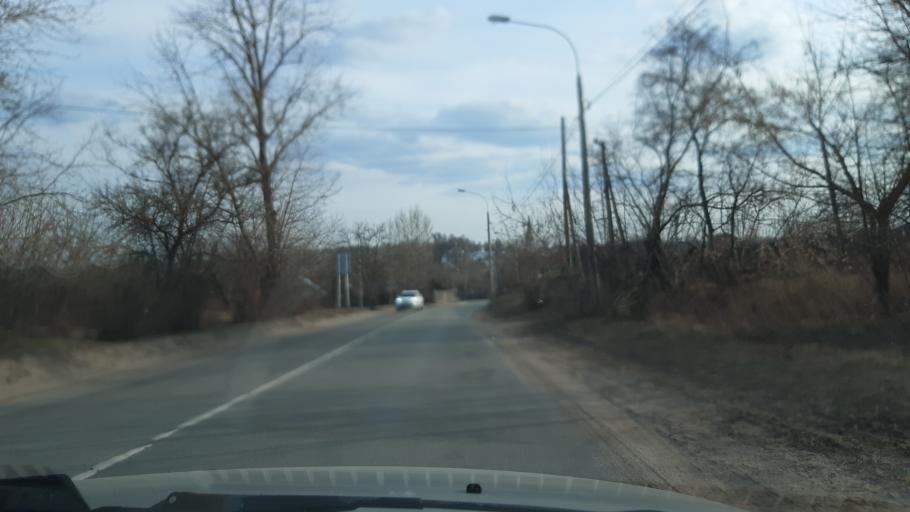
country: RU
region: Vladimir
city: Nikologory
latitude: 56.1464
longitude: 41.9933
